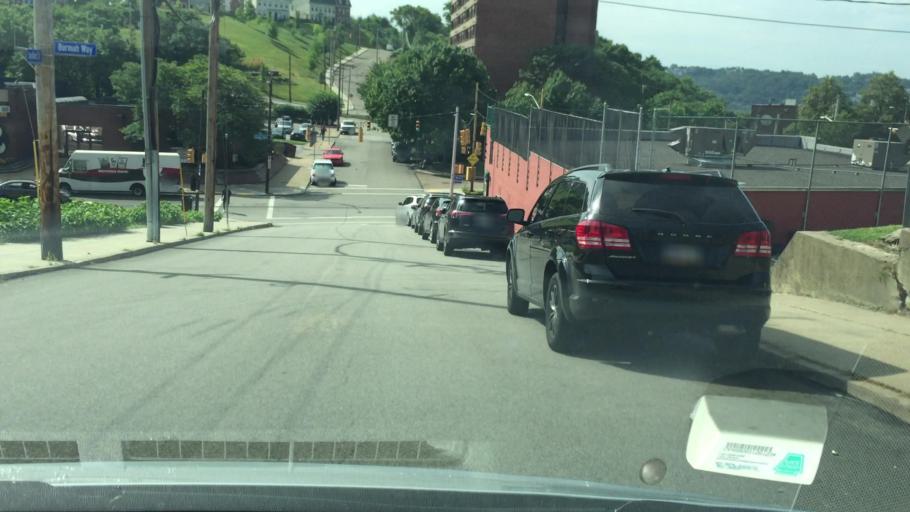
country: US
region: Pennsylvania
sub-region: Allegheny County
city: Pittsburgh
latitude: 40.4441
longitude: -79.9807
